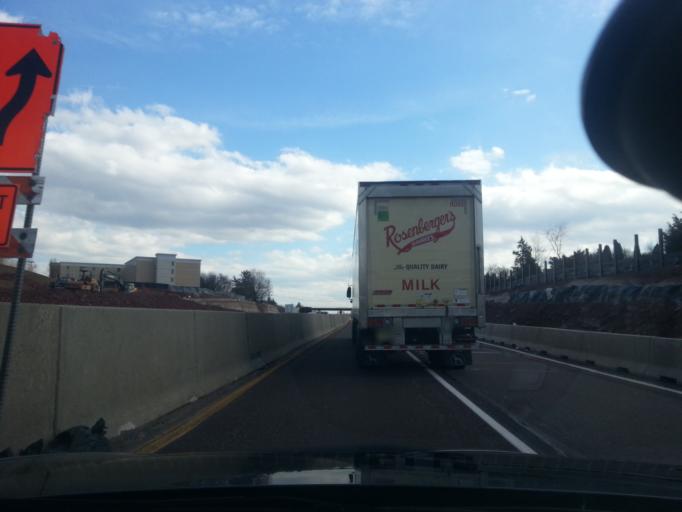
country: US
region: Pennsylvania
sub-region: Montgomery County
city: Kulpsville
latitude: 40.2461
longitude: -75.3447
